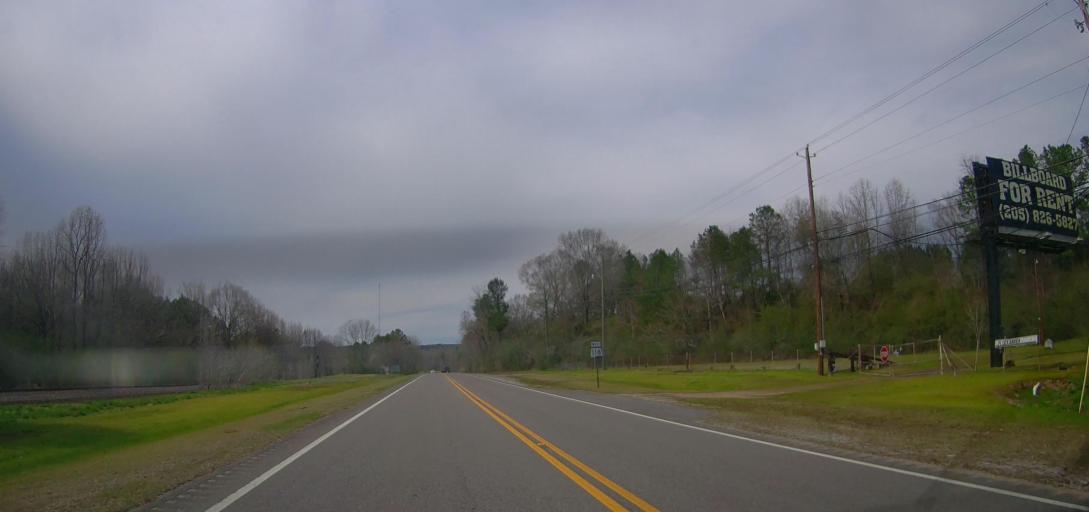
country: US
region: Alabama
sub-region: Walker County
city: Carbon Hill
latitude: 33.8922
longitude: -87.5348
